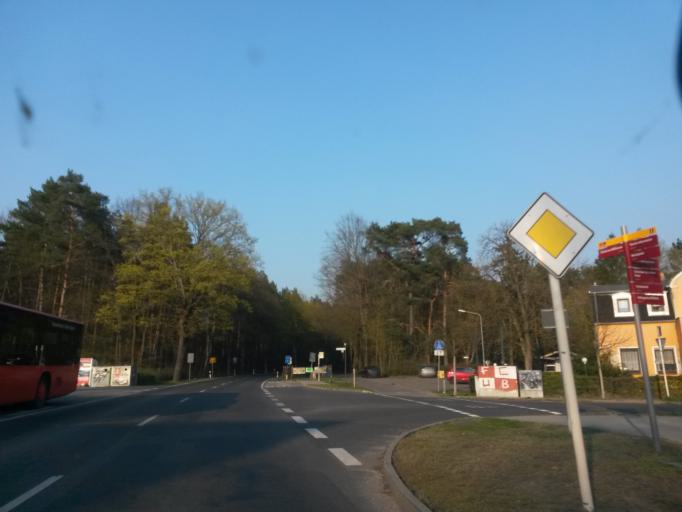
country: DE
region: Brandenburg
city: Grunheide
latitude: 52.4353
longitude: 13.8365
